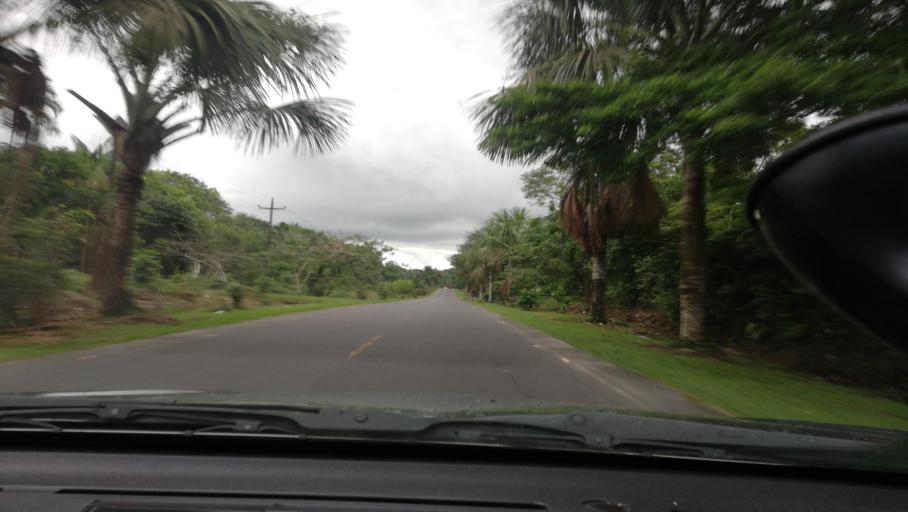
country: PE
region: Loreto
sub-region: Provincia de Maynas
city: San Juan
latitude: -3.9601
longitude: -73.4126
